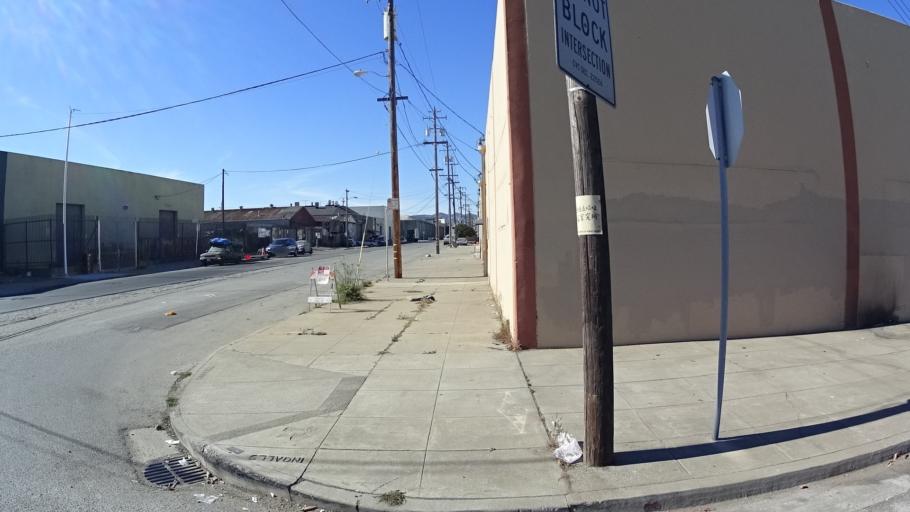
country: US
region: California
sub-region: San Mateo County
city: Brisbane
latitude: 37.7229
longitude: -122.3895
